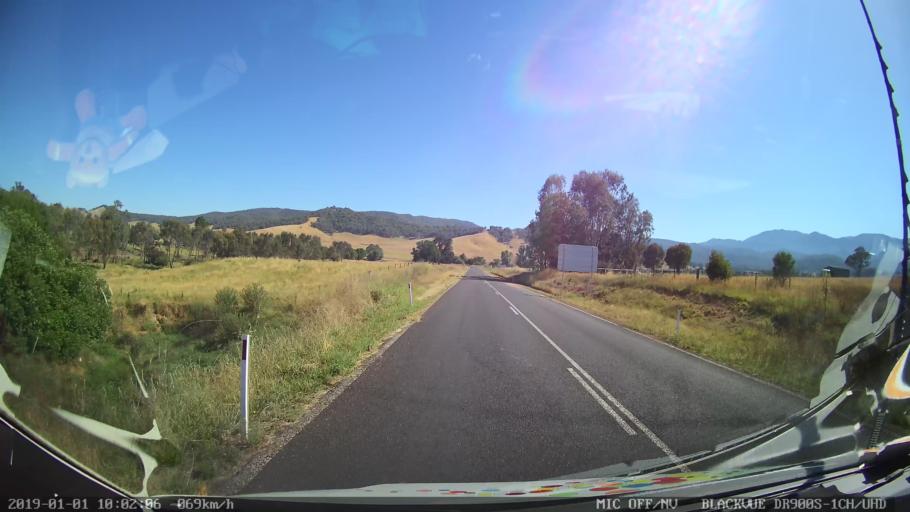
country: AU
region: New South Wales
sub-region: Snowy River
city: Jindabyne
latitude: -36.1847
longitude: 148.1014
